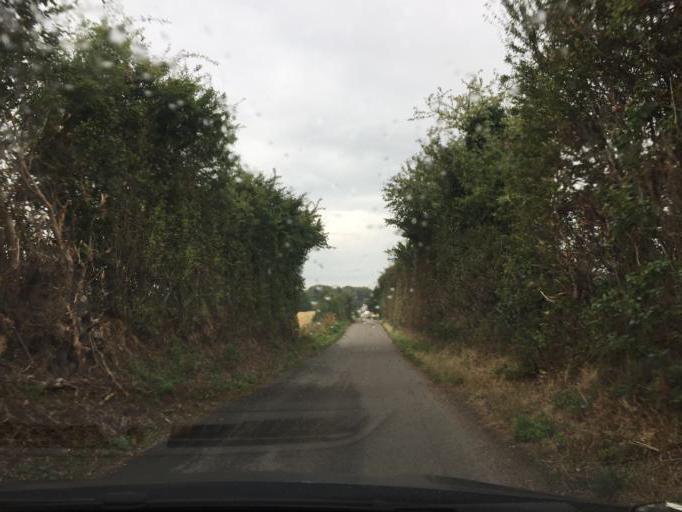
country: DK
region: South Denmark
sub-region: Assens Kommune
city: Harby
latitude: 55.2074
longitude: 10.0053
